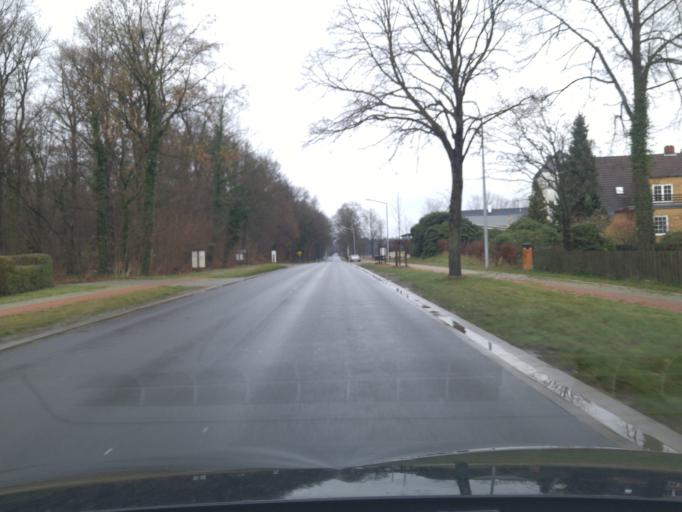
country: DE
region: Lower Saxony
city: Sprakensehl
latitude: 52.7696
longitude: 10.4935
